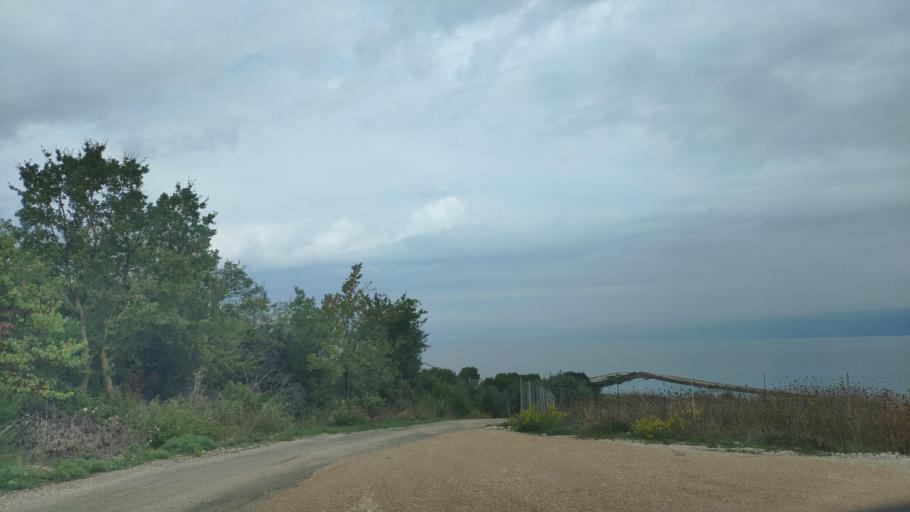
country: GR
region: West Greece
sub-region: Nomos Aitolias kai Akarnanias
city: Monastirakion
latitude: 38.9249
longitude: 21.0221
